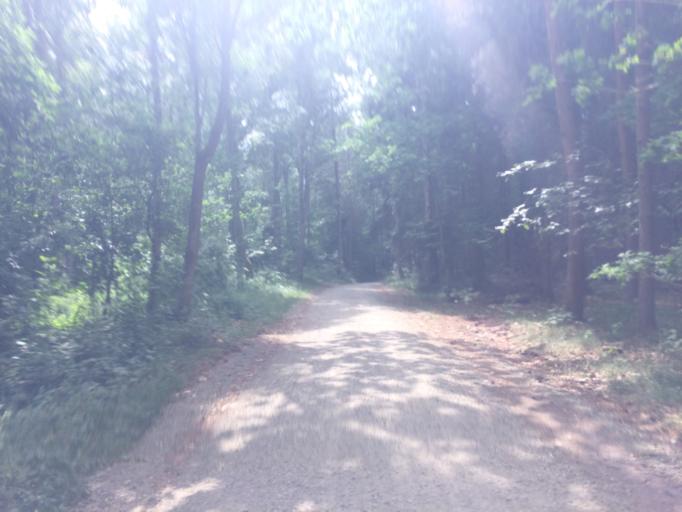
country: DK
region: Capital Region
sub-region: Bornholm Kommune
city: Ronne
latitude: 55.1268
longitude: 14.7121
